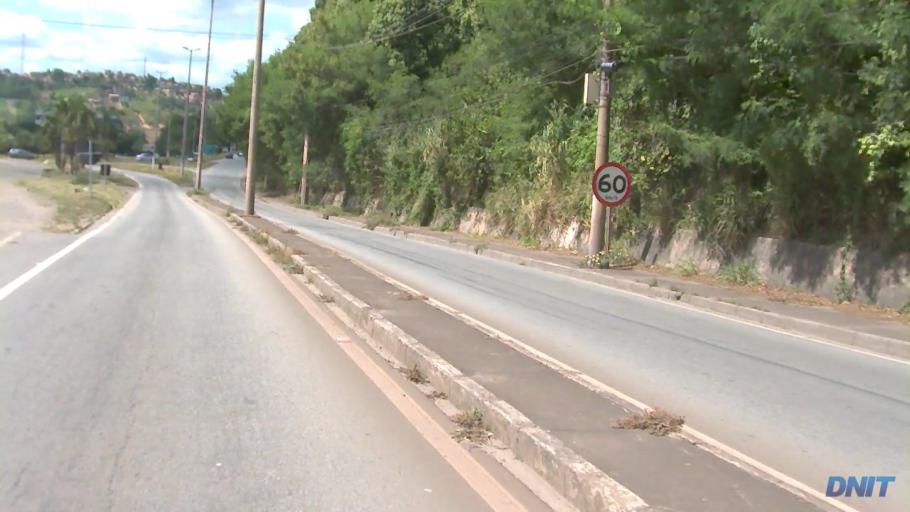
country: BR
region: Minas Gerais
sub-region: Coronel Fabriciano
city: Coronel Fabriciano
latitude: -19.5280
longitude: -42.6436
